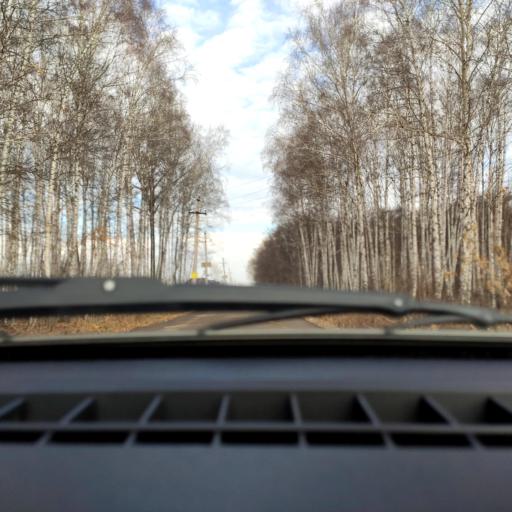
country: RU
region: Bashkortostan
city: Ufa
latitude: 54.6279
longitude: 55.8903
